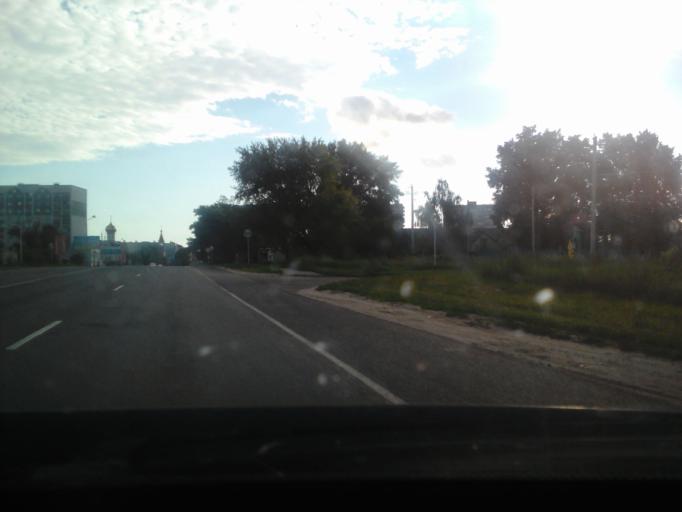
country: RU
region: Kursk
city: Kurchatov
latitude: 51.6562
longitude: 35.7005
